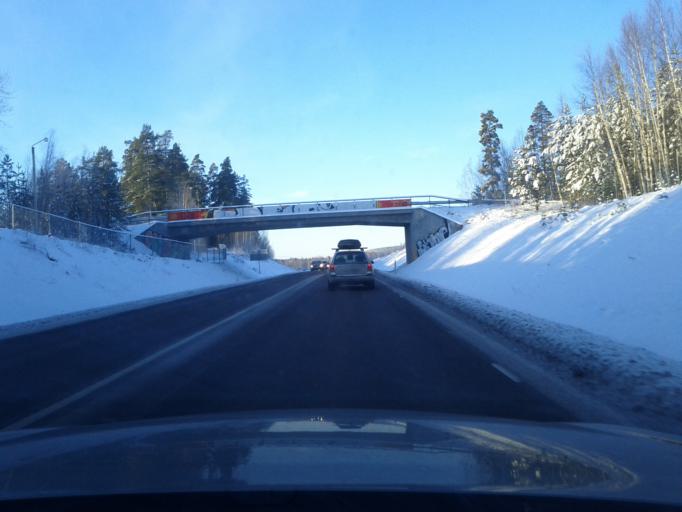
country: SE
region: Dalarna
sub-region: Faluns Kommun
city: Falun
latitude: 60.6027
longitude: 15.6758
